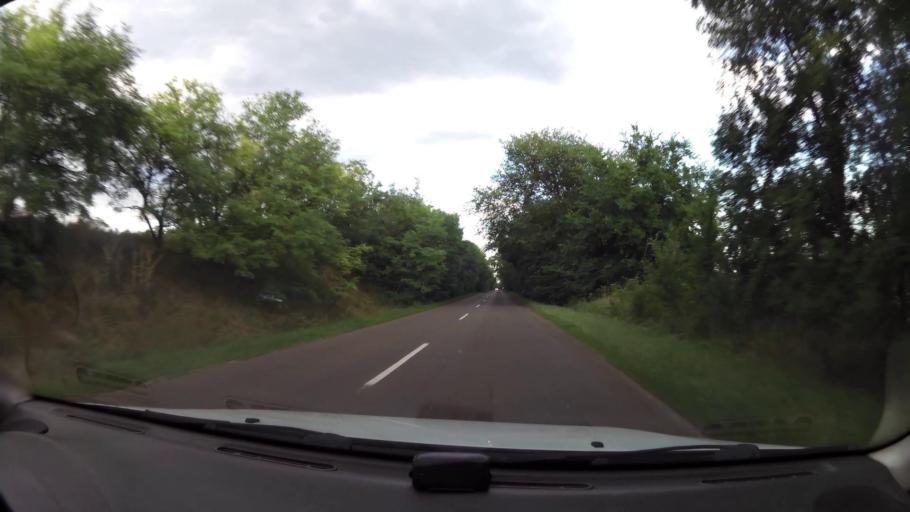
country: HU
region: Pest
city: Tapiosag
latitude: 47.3950
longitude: 19.6364
